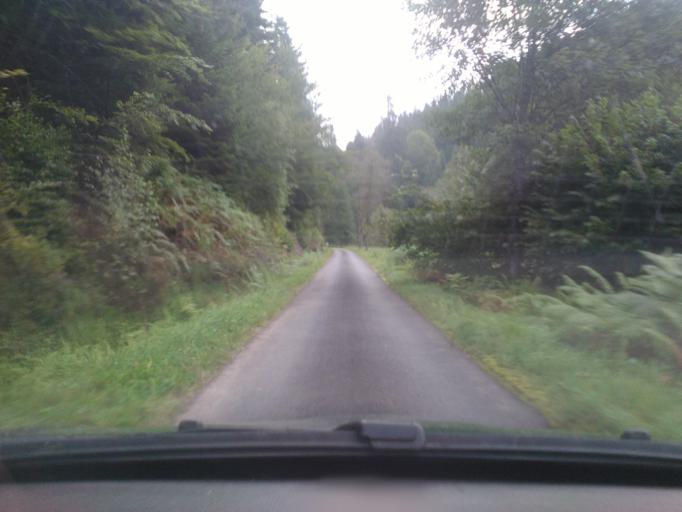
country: FR
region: Lorraine
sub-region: Departement des Vosges
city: Senones
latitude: 48.4226
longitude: 6.9491
